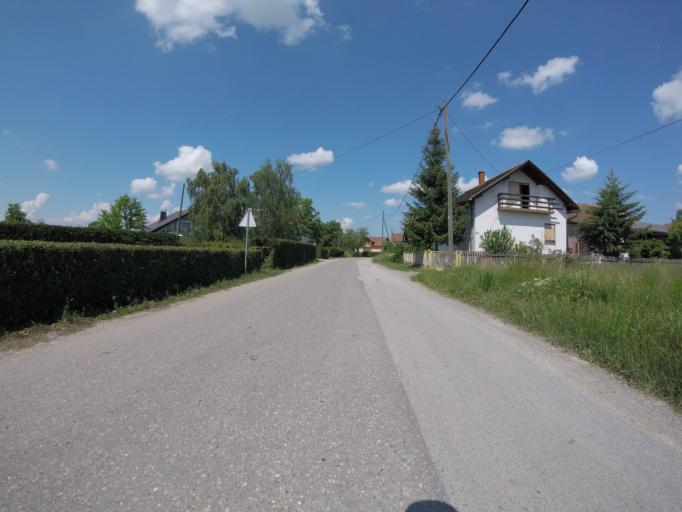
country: HR
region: Zagrebacka
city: Gradici
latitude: 45.6762
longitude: 16.0657
